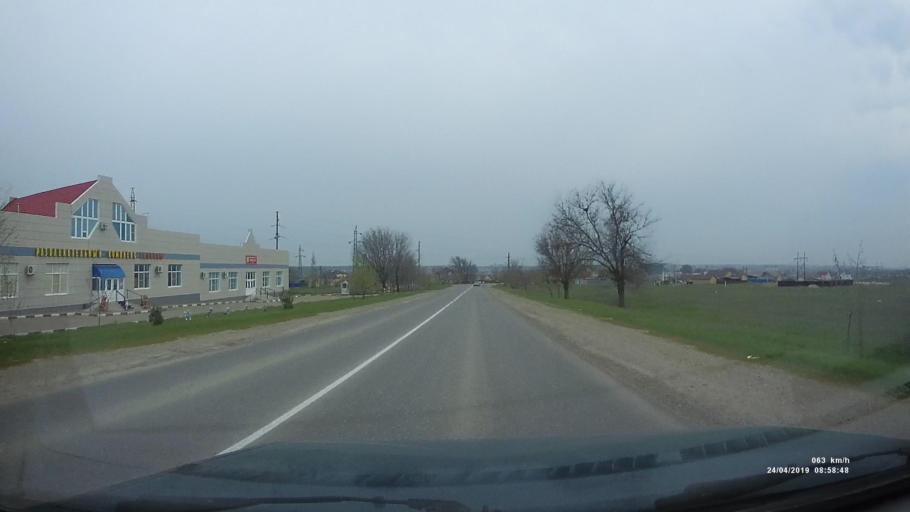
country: RU
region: Kalmykiya
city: Arshan'
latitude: 46.3105
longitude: 44.2019
